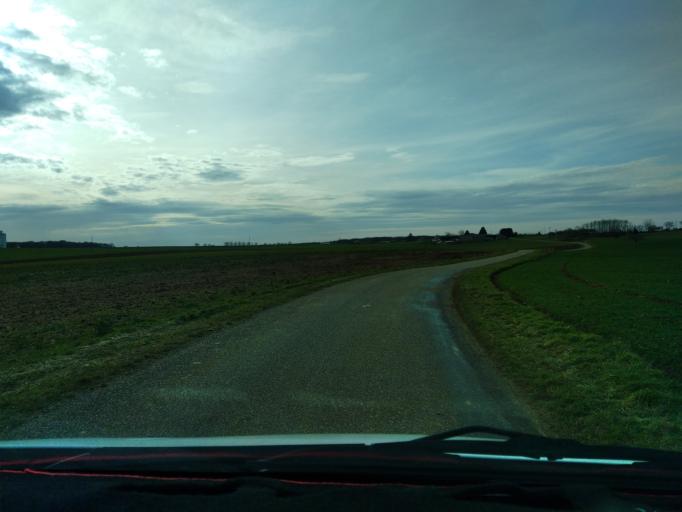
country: FR
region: Franche-Comte
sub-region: Departement de la Haute-Saone
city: Marnay
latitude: 47.3617
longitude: 5.6895
